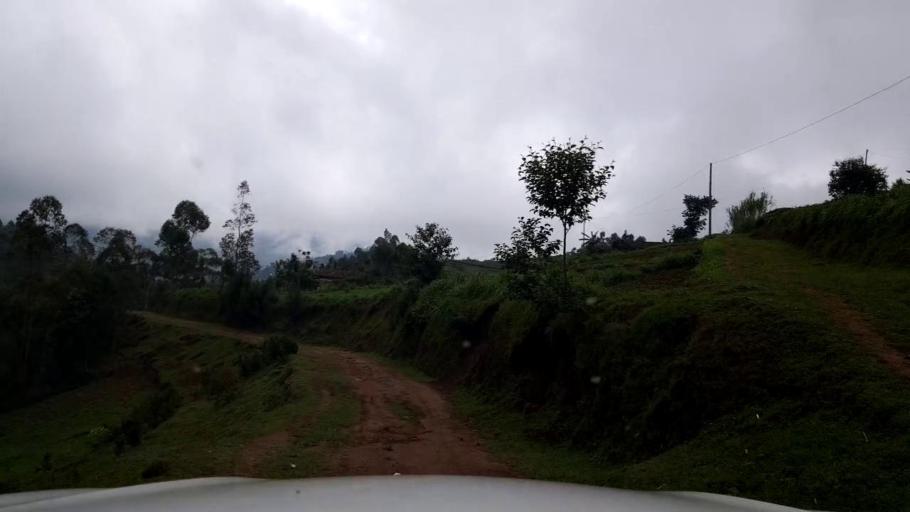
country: RW
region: Northern Province
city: Musanze
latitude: -1.5952
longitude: 29.7707
